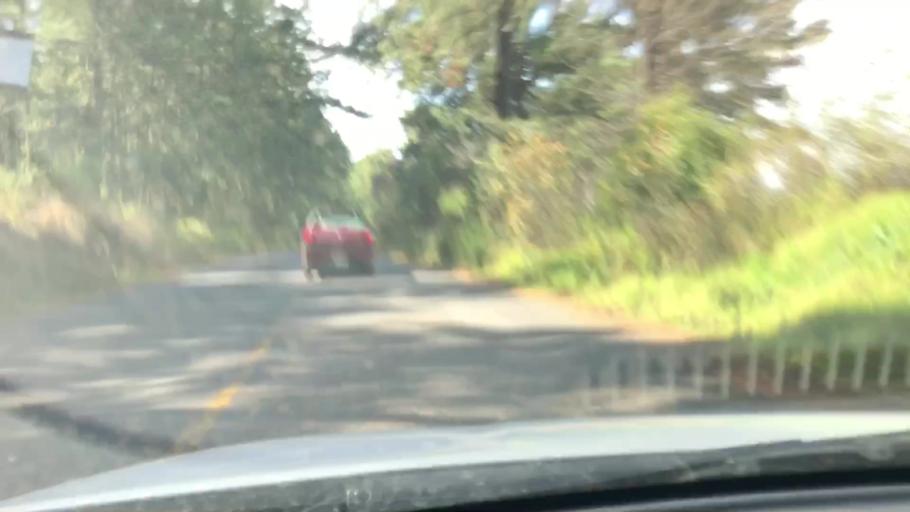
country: MX
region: Jalisco
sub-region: Amacueca
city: Tepec
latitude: 20.0809
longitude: -103.7129
